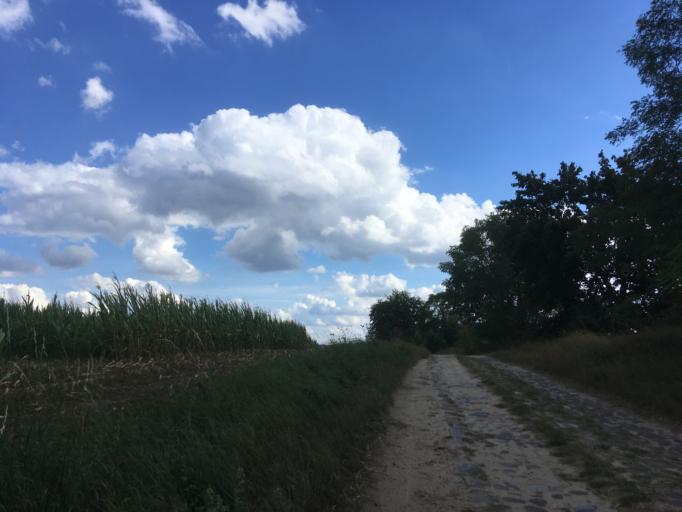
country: DE
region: Brandenburg
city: Angermunde
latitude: 52.9367
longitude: 14.0045
